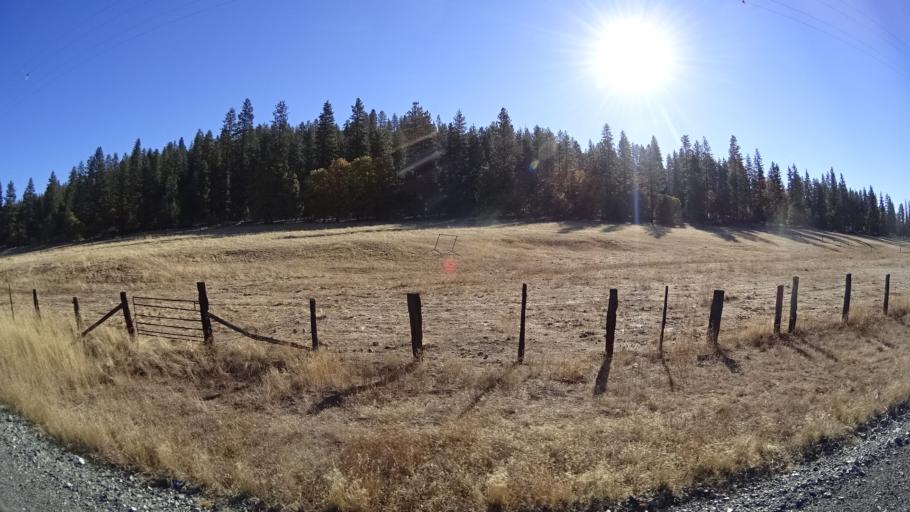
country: US
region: California
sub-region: Siskiyou County
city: Yreka
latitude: 41.4692
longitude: -122.8823
